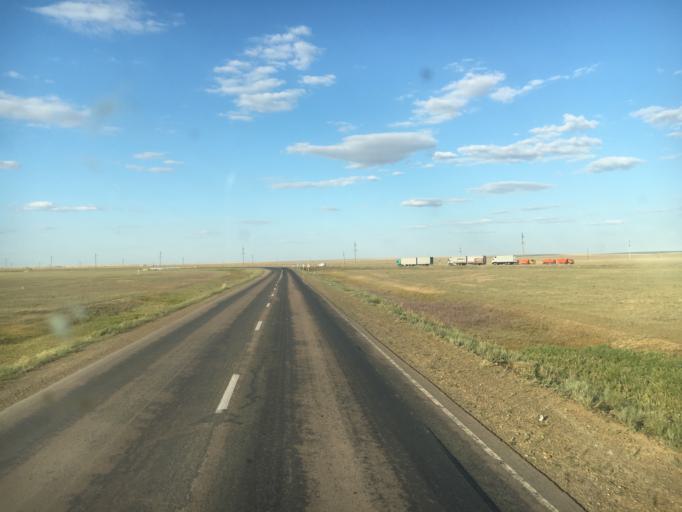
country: RU
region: Orenburg
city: Dombarovskiy
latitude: 49.9713
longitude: 60.1300
